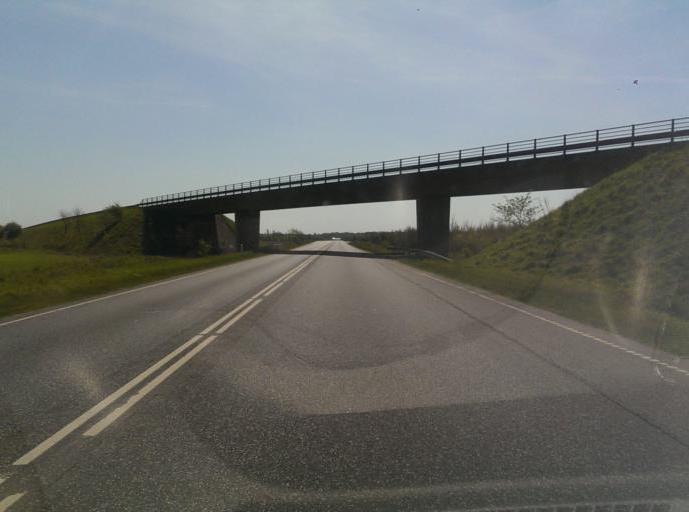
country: DK
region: South Denmark
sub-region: Esbjerg Kommune
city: Bramming
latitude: 55.4053
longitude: 8.7243
